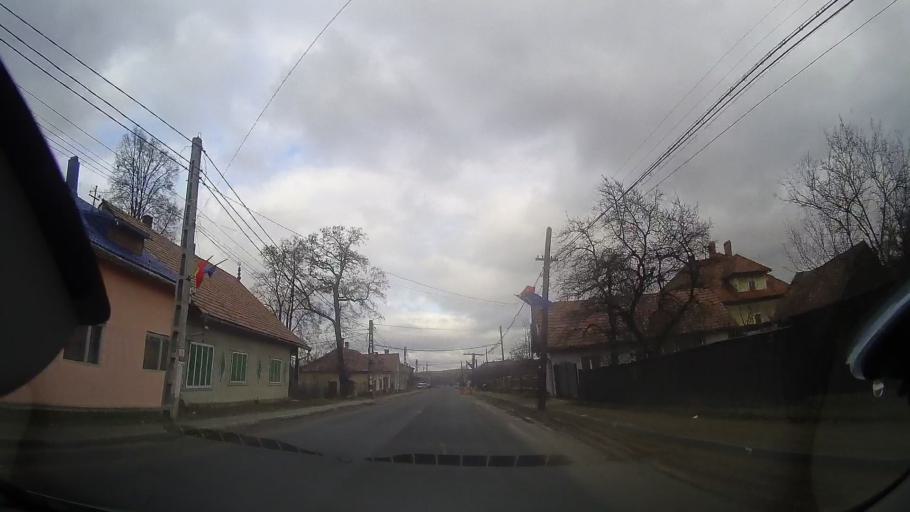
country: RO
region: Cluj
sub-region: Comuna Calatele
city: Calatele
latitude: 46.7663
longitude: 23.0083
